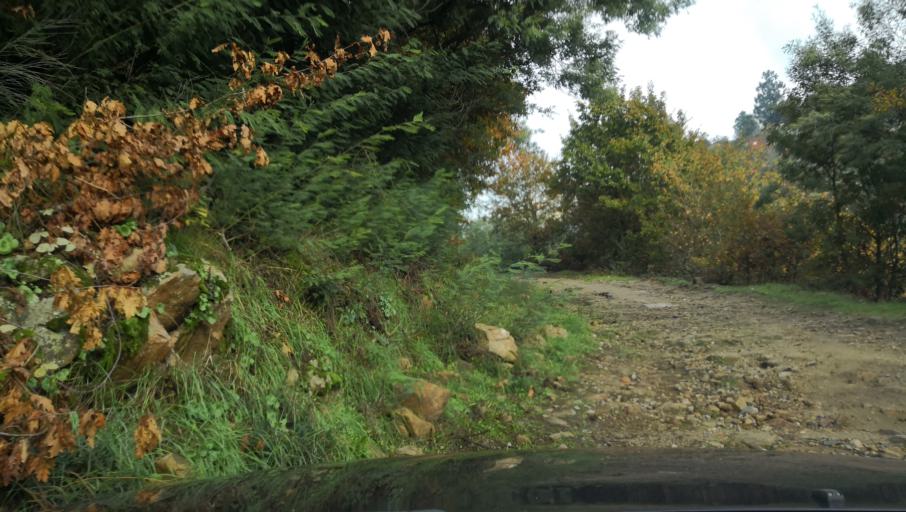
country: PT
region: Vila Real
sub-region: Vila Real
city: Vila Real
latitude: 41.2897
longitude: -7.7493
